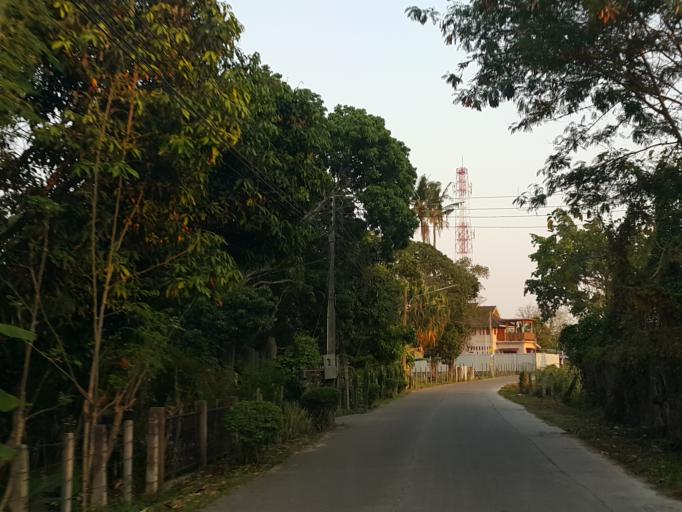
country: TH
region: Chiang Mai
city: San Sai
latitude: 18.8804
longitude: 98.9666
